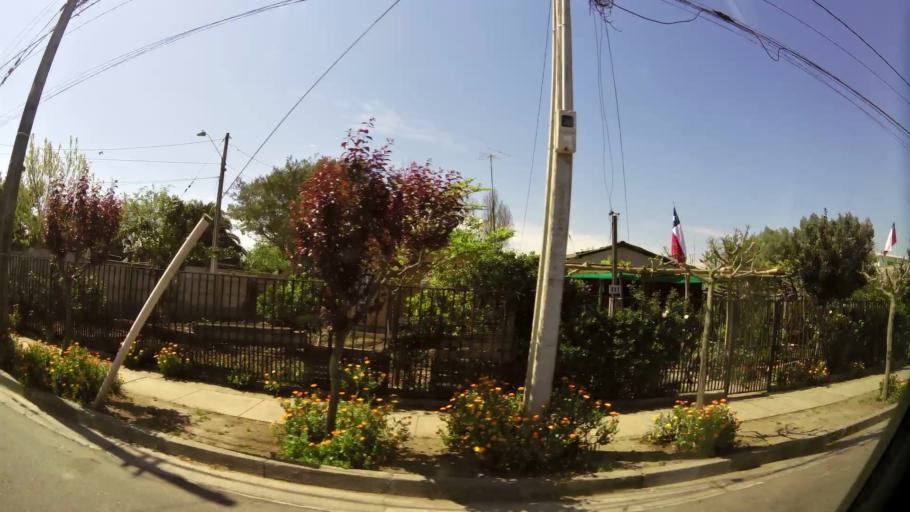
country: CL
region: Santiago Metropolitan
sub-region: Provincia de Talagante
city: Talagante
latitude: -33.6582
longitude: -70.9191
